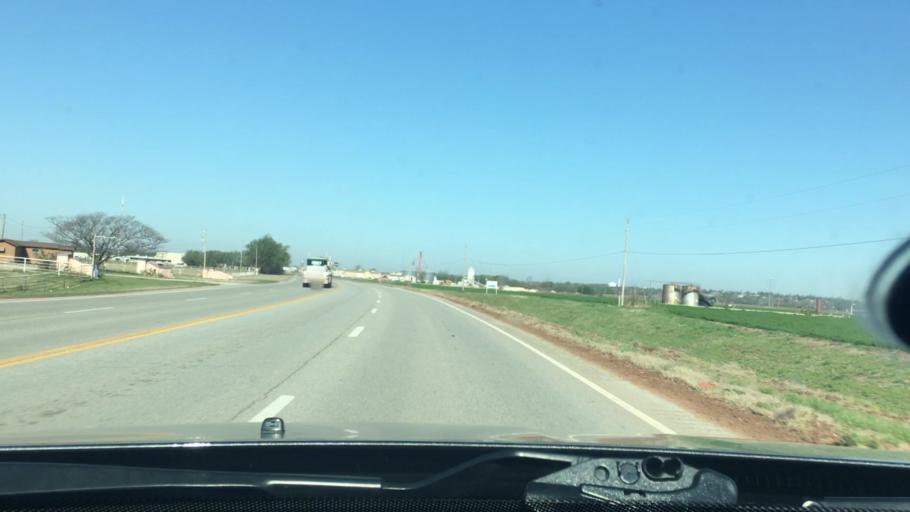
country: US
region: Oklahoma
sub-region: Garvin County
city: Lindsay
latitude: 34.8352
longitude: -97.5854
